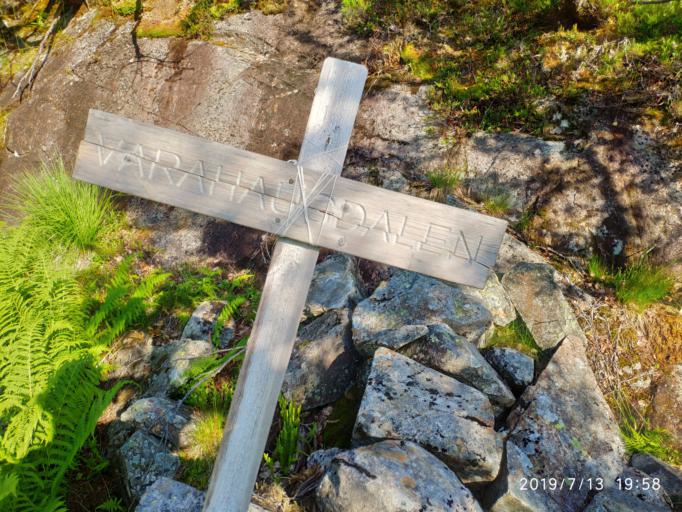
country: NO
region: Rogaland
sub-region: Sauda
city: Sauda
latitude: 59.8402
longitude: 6.3476
